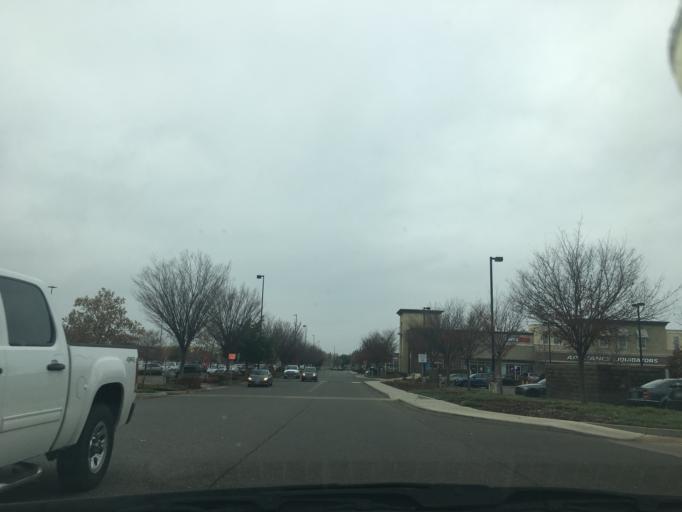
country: US
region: California
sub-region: Yolo County
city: West Sacramento
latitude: 38.5894
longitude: -121.5487
